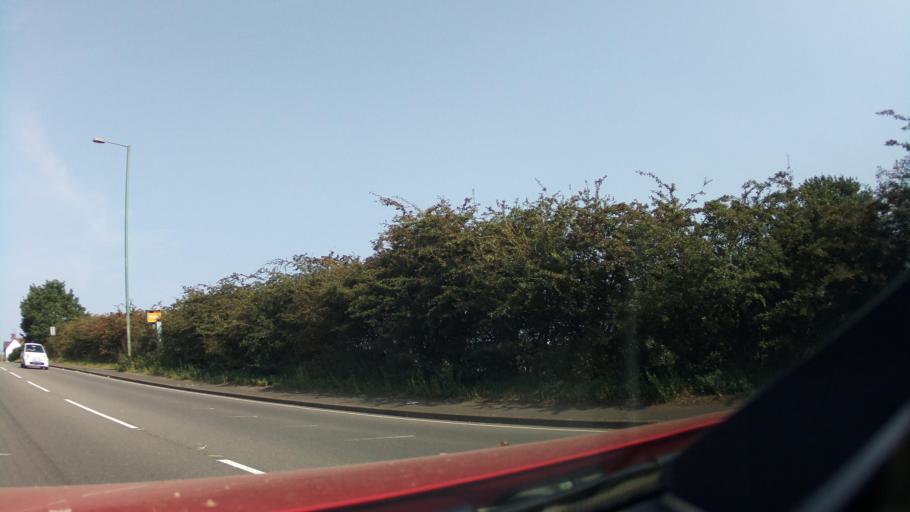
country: GB
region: England
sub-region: Walsall
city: Aldridge
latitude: 52.6186
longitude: -1.8898
